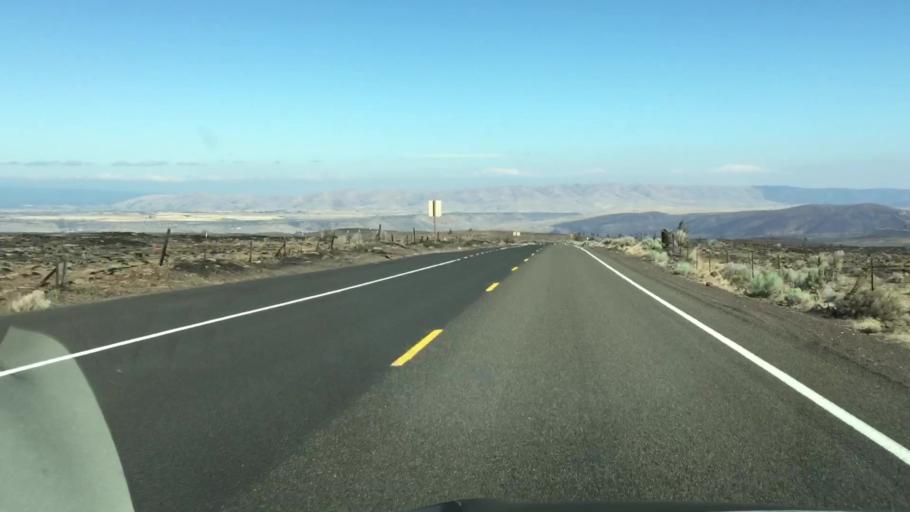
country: US
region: Oregon
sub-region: Jefferson County
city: Warm Springs
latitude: 45.1038
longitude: -121.0387
